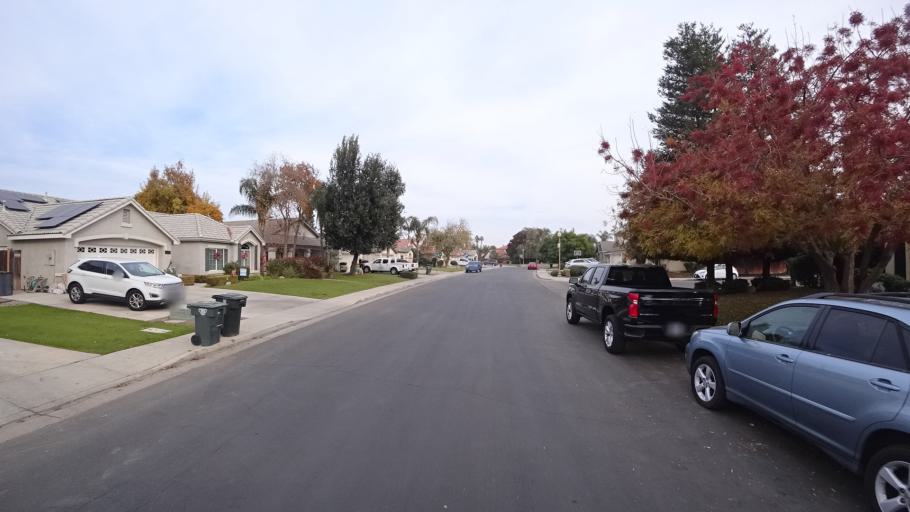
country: US
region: California
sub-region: Kern County
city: Rosedale
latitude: 35.3445
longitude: -119.1306
